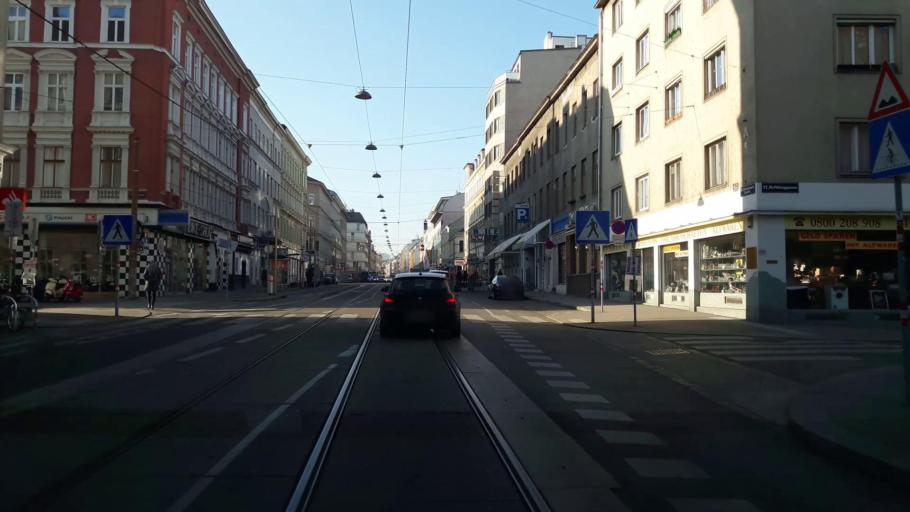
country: AT
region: Vienna
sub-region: Wien Stadt
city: Vienna
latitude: 48.2148
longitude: 16.3360
